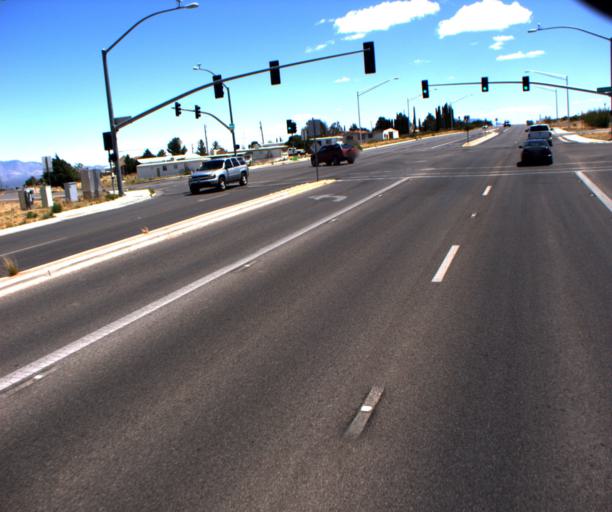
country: US
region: Arizona
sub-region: Cochise County
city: Sierra Vista Southeast
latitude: 31.4382
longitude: -110.2485
